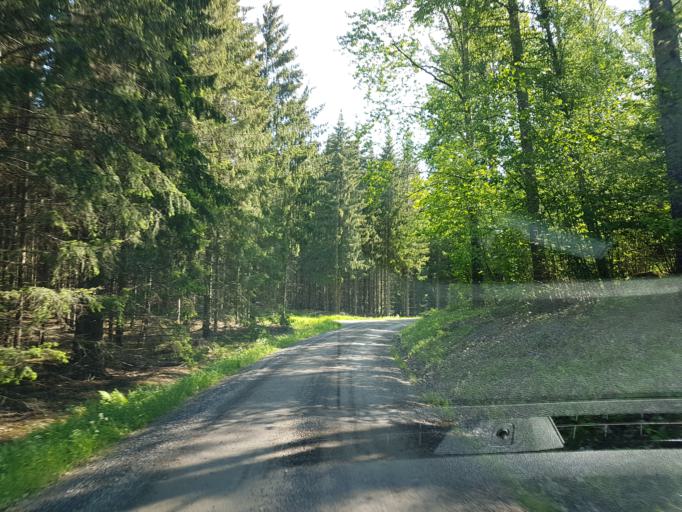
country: SE
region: OEstergoetland
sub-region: Atvidabergs Kommun
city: Atvidaberg
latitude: 58.1851
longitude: 16.1234
